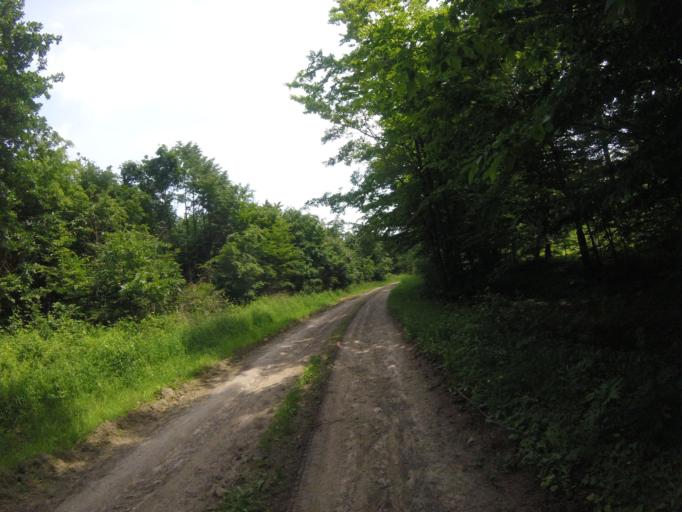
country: HU
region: Zala
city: Turje
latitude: 46.9093
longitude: 17.1839
